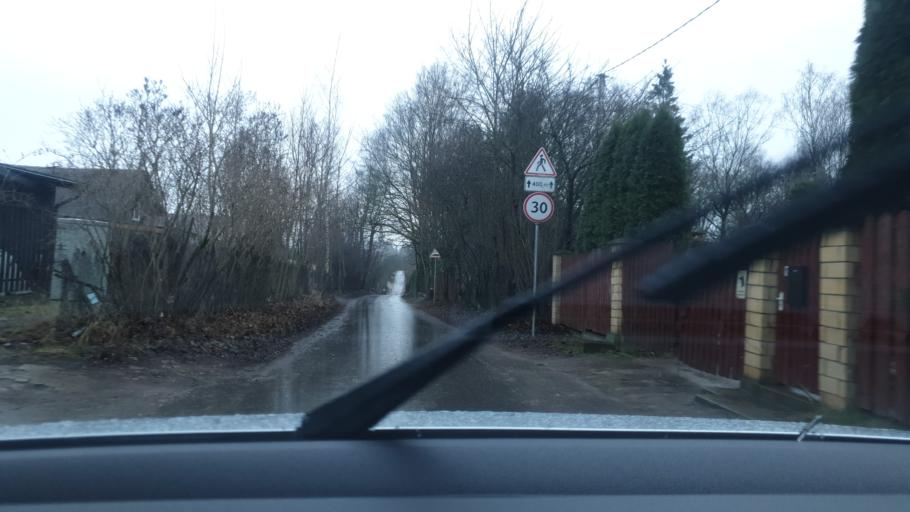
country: LT
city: Skaidiskes
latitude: 54.7048
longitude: 25.4089
